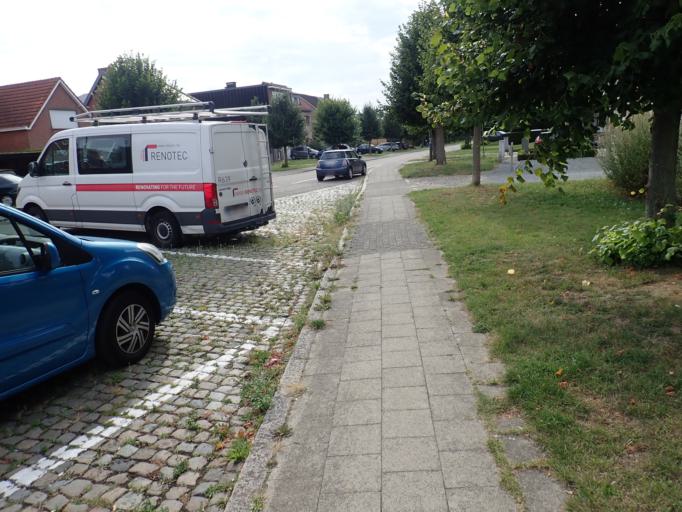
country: BE
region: Flanders
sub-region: Provincie Antwerpen
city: Wommelgem
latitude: 51.2074
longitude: 4.5108
